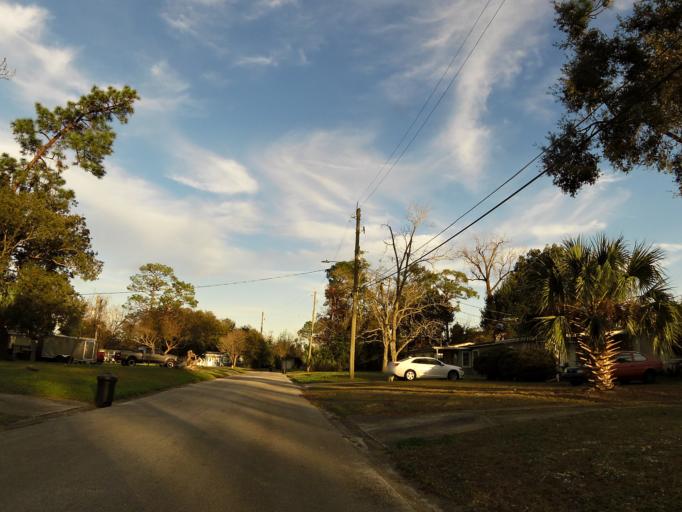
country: US
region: Florida
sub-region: Duval County
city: Jacksonville
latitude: 30.2889
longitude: -81.6391
